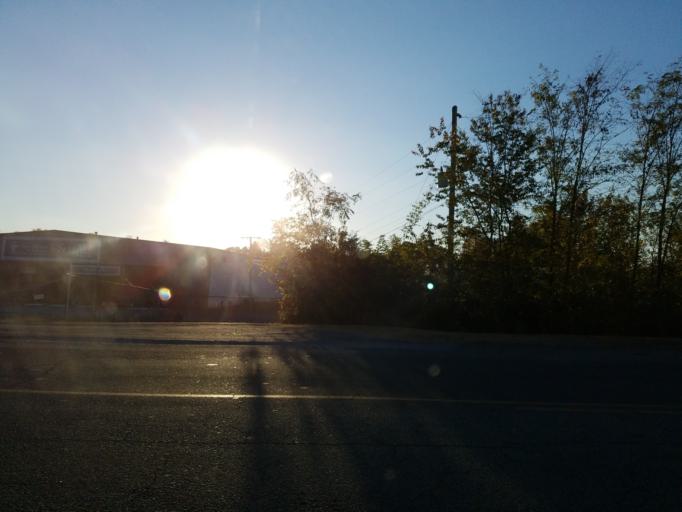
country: US
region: Georgia
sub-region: Gordon County
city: Calhoun
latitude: 34.4870
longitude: -84.9553
